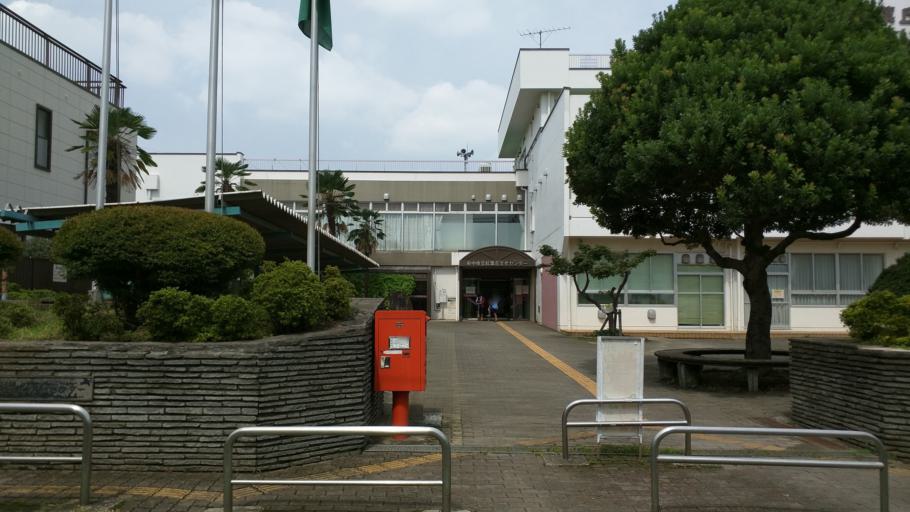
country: JP
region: Tokyo
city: Kokubunji
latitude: 35.6761
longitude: 139.5092
